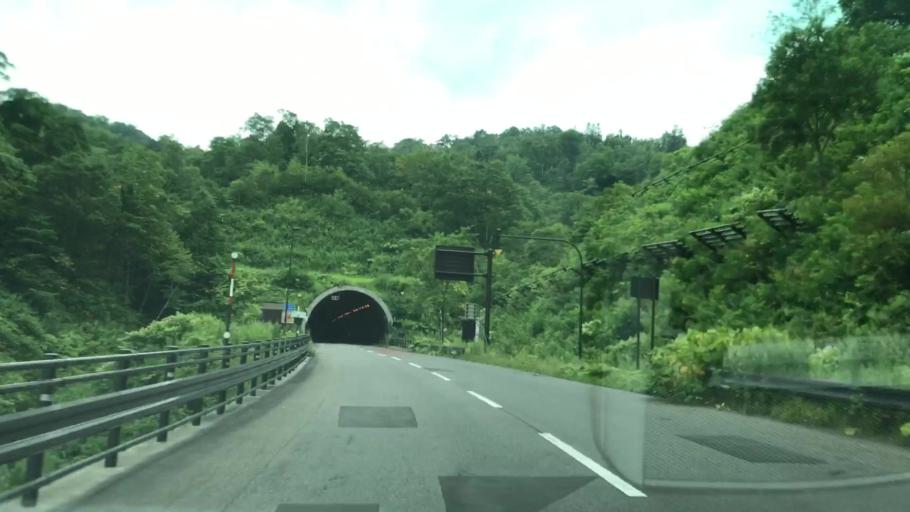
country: JP
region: Hokkaido
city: Yoichi
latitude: 42.9817
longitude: 140.8720
